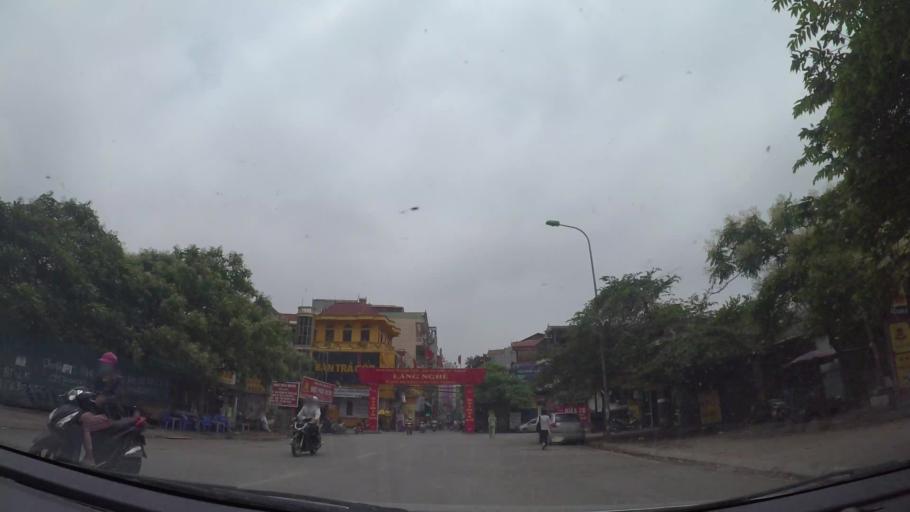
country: VN
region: Ha Noi
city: Tay Ho
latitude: 21.0690
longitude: 105.8026
